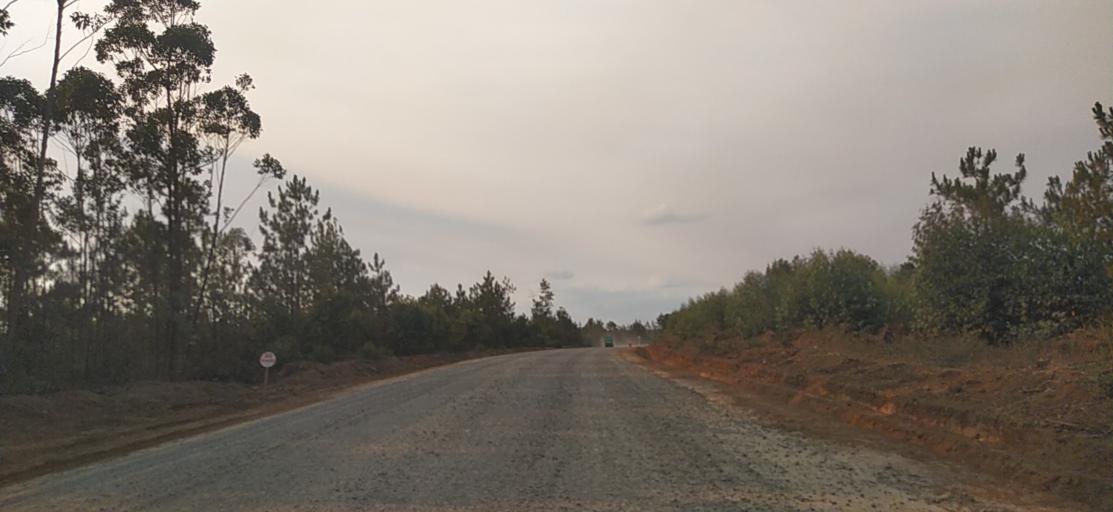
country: MG
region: Alaotra Mangoro
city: Moramanga
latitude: -18.5583
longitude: 48.2591
